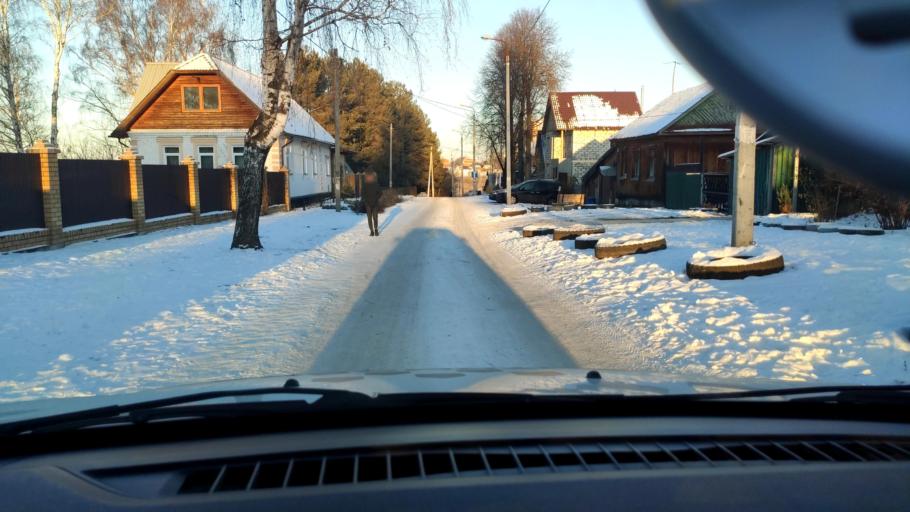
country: RU
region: Perm
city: Perm
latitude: 58.0538
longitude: 56.3338
